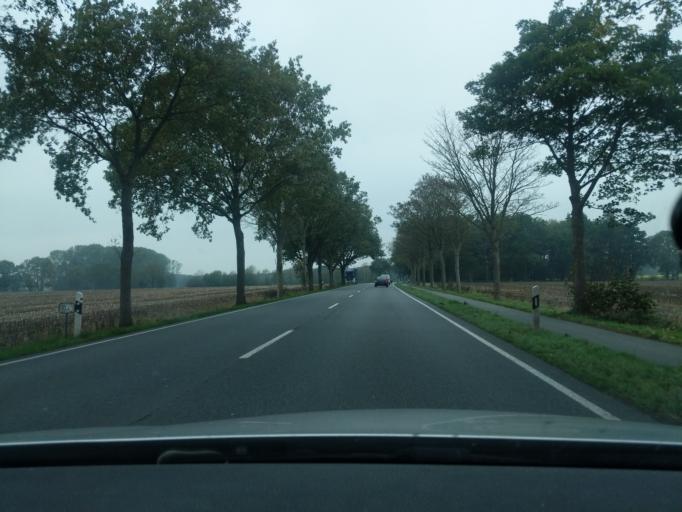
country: DE
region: Lower Saxony
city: Heinbockel
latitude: 53.5947
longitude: 9.3321
